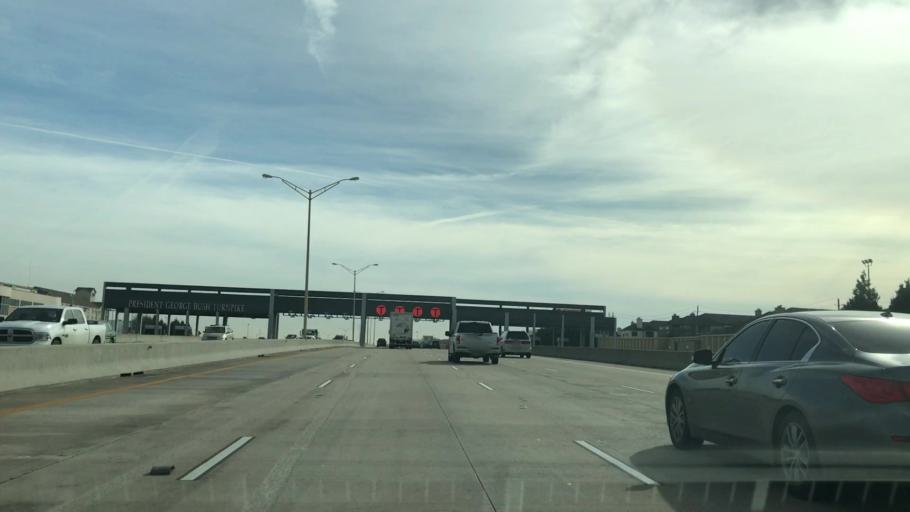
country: US
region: Texas
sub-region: Dallas County
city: Addison
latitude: 33.0032
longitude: -96.7781
